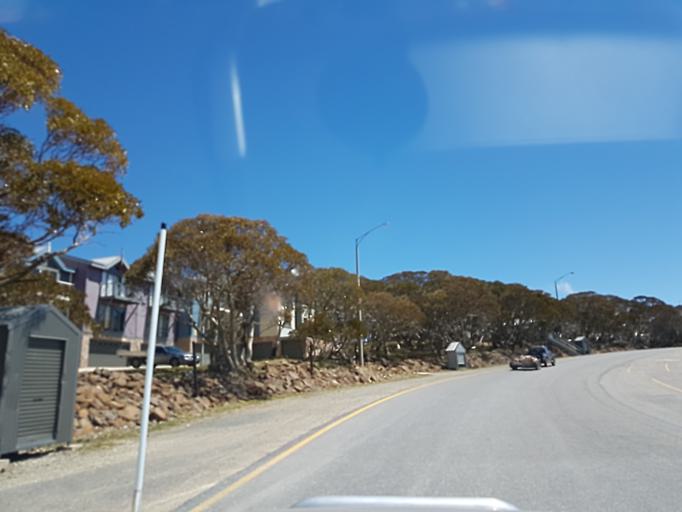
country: AU
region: Victoria
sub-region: Alpine
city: Mount Beauty
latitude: -36.9938
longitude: 147.1512
